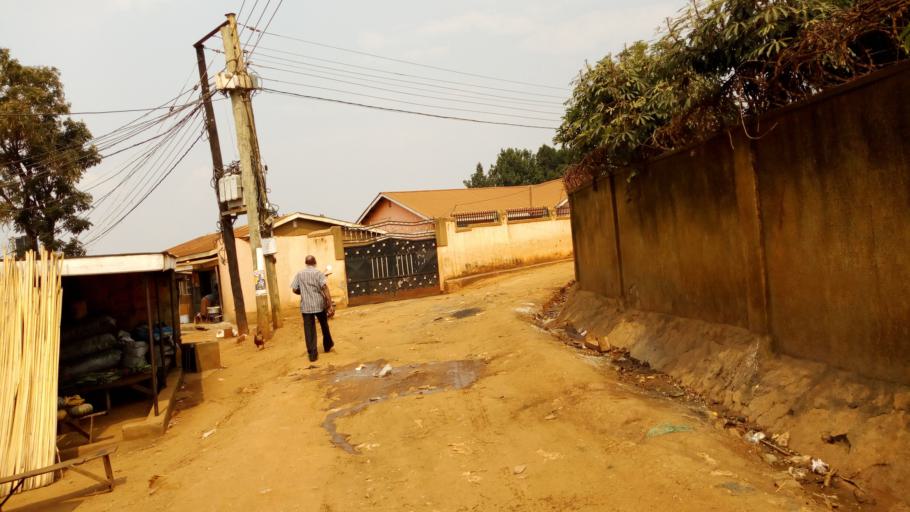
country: UG
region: Central Region
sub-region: Wakiso District
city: Kireka
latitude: 0.3239
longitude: 32.6426
